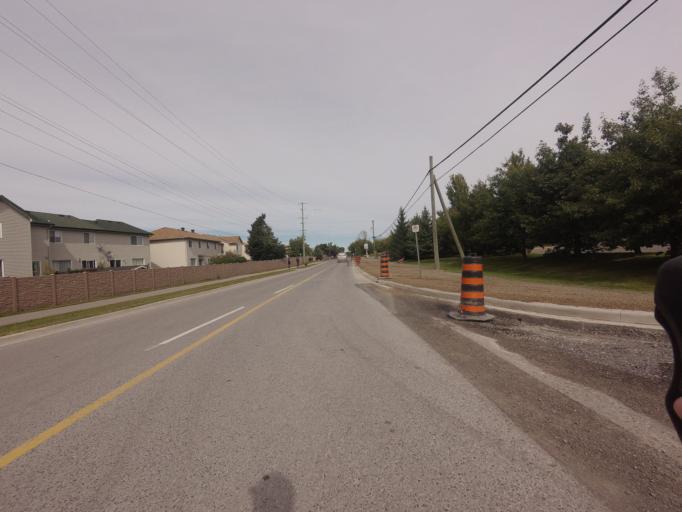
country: CA
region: Ontario
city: Carleton Place
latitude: 45.1440
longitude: -76.1309
